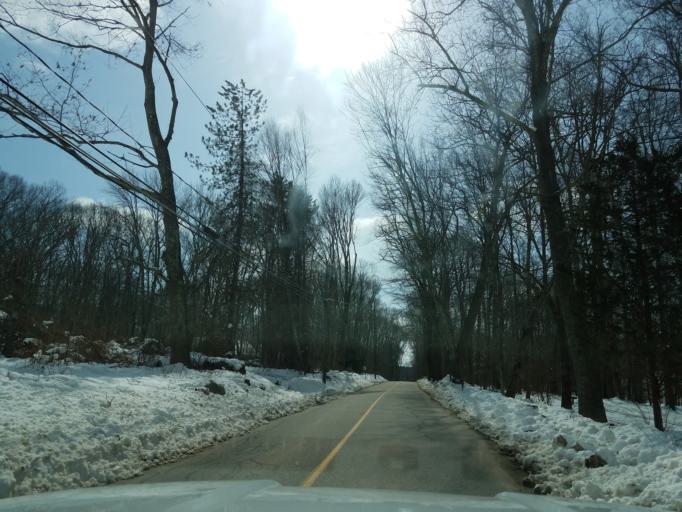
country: US
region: Connecticut
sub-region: Tolland County
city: Coventry Lake
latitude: 41.7245
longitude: -72.3560
